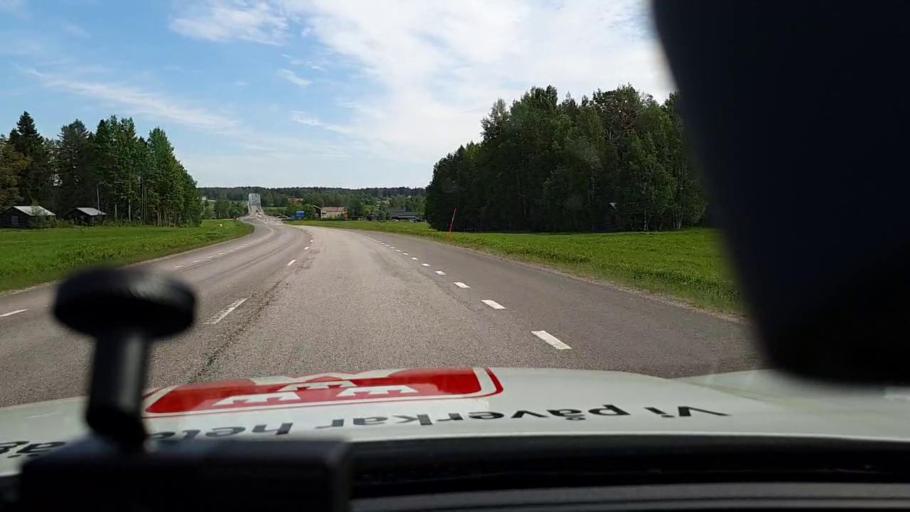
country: SE
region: Norrbotten
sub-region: Lulea Kommun
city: Gammelstad
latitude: 65.5838
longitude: 22.0214
